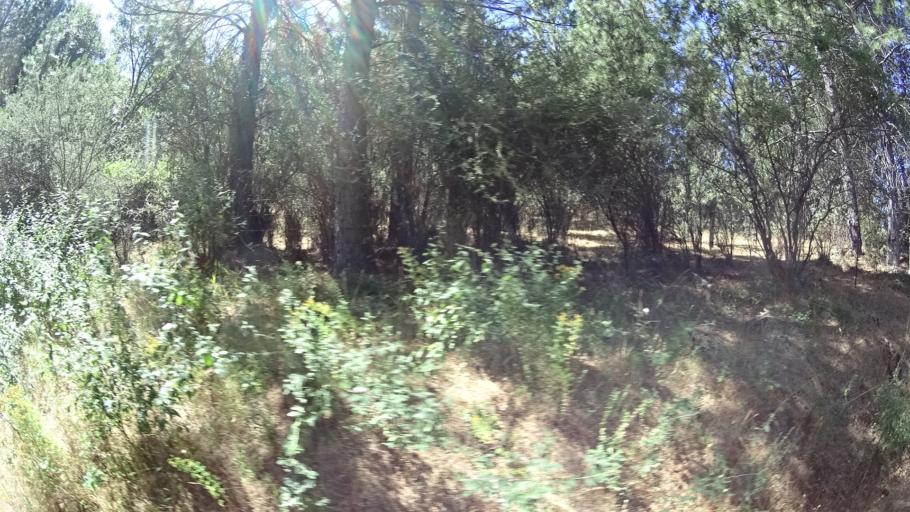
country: US
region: California
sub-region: Calaveras County
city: Mountain Ranch
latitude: 38.3394
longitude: -120.4785
